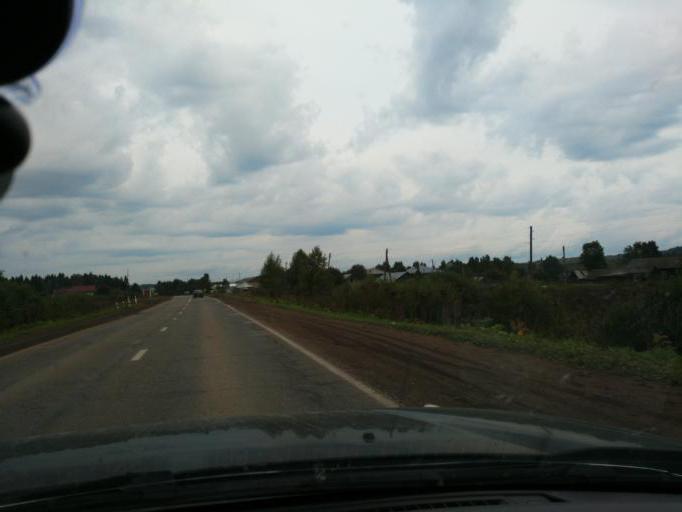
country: RU
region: Perm
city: Chernushka
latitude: 56.7299
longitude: 56.1771
